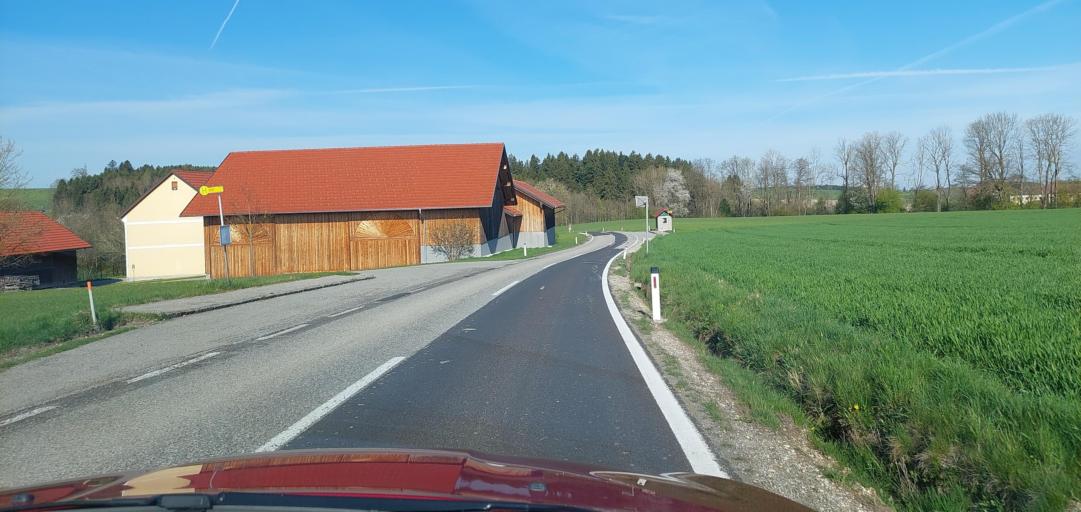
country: AT
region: Upper Austria
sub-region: Politischer Bezirk Ried im Innkreis
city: Ried im Innkreis
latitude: 48.1767
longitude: 13.5488
